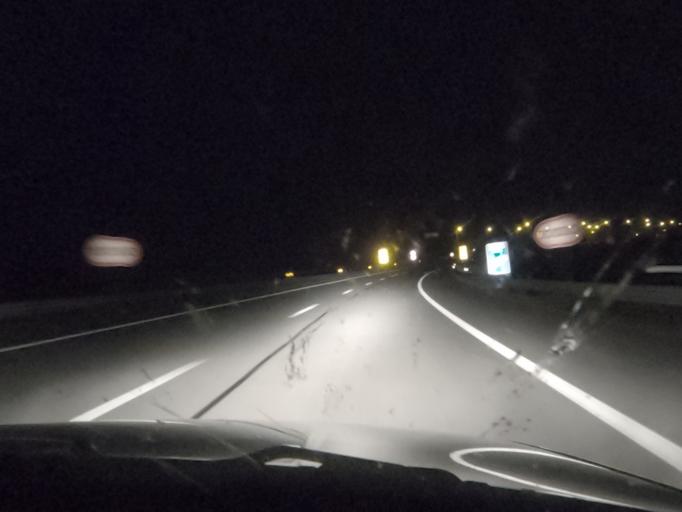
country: PT
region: Evora
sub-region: Estremoz
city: Estremoz
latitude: 38.8395
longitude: -7.6128
